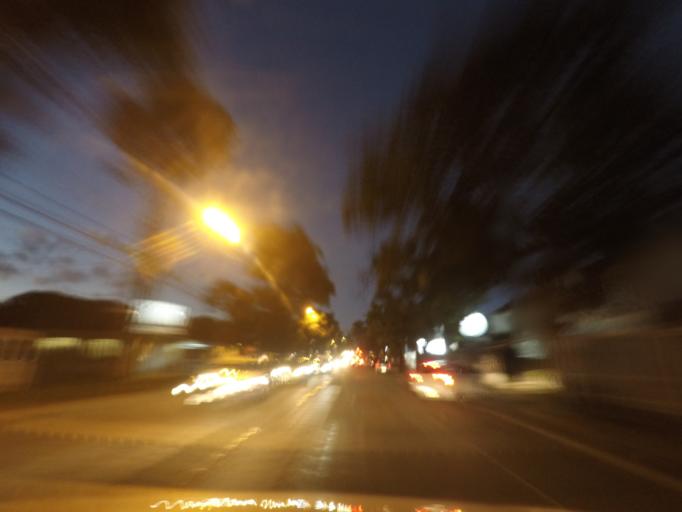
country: BR
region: Parana
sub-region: Curitiba
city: Curitiba
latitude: -25.4579
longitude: -49.2788
